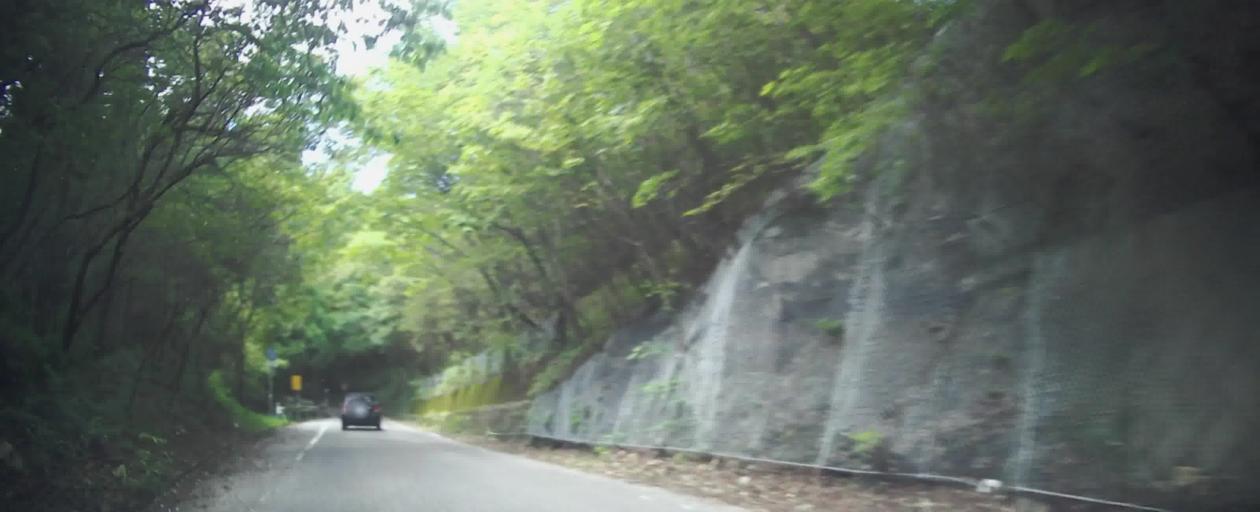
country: JP
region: Gunma
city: Shibukawa
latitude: 36.4589
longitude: 138.8951
